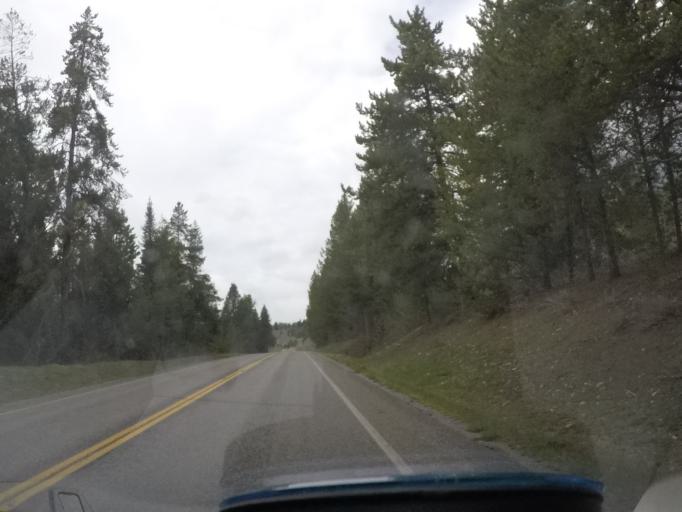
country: US
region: Wyoming
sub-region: Teton County
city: Jackson
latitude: 43.8615
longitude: -110.5337
